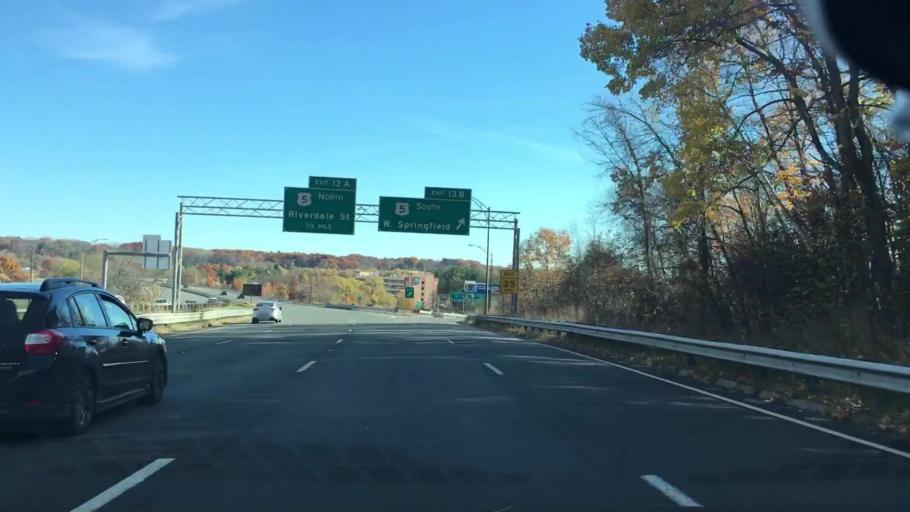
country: US
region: Massachusetts
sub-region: Hampden County
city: Chicopee
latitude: 42.1370
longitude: -72.6320
